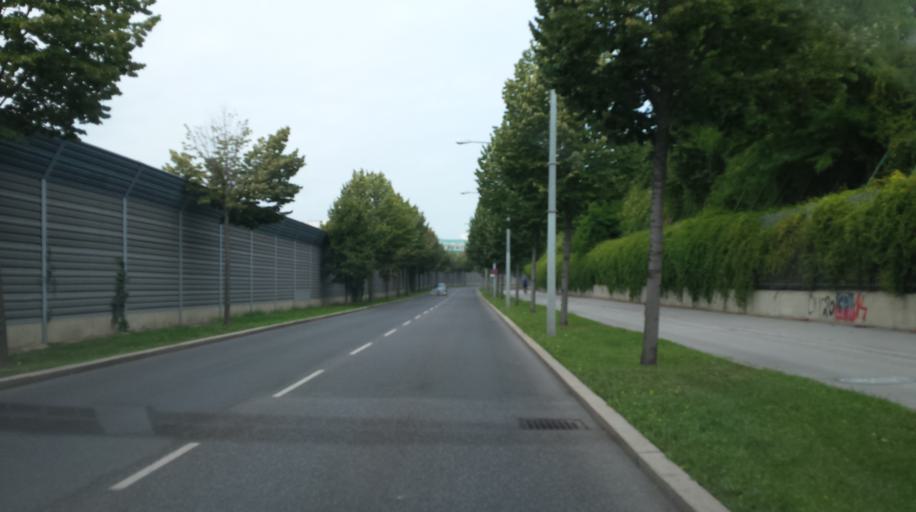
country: AT
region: Lower Austria
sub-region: Politischer Bezirk Wien-Umgebung
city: Gerasdorf bei Wien
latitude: 48.2446
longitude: 16.4303
